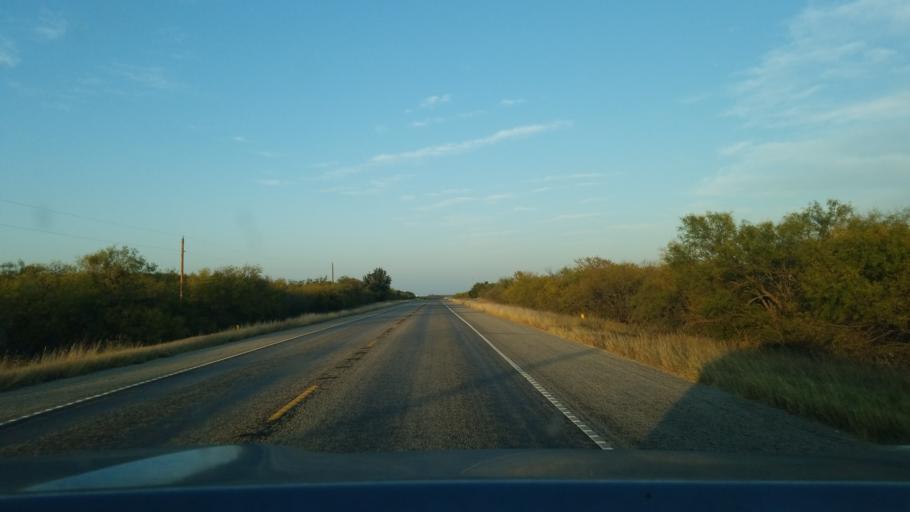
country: US
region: Texas
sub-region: Eastland County
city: Cisco
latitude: 32.4396
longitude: -98.9179
